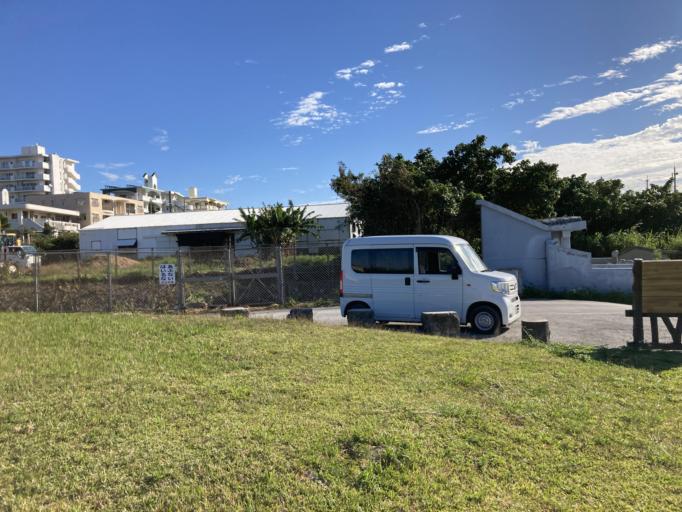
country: JP
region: Okinawa
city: Chatan
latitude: 26.3702
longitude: 127.7351
